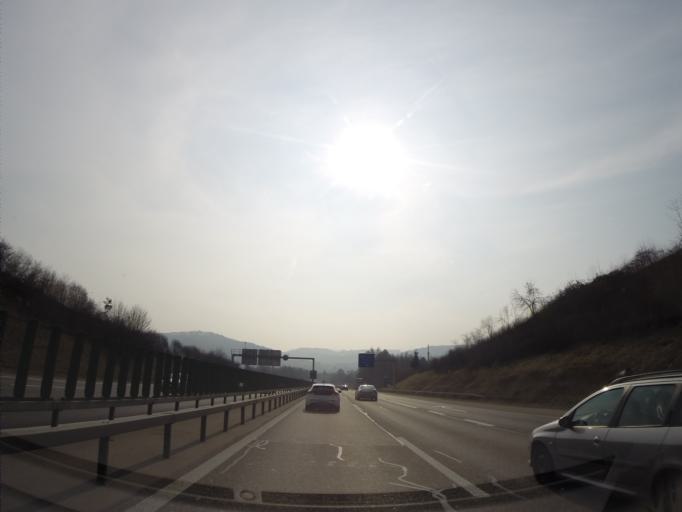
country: CH
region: Zurich
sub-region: Bezirk Winterthur
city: Wuelflingen (Kreis 6) / Lindenplatz
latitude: 47.5172
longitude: 8.6943
